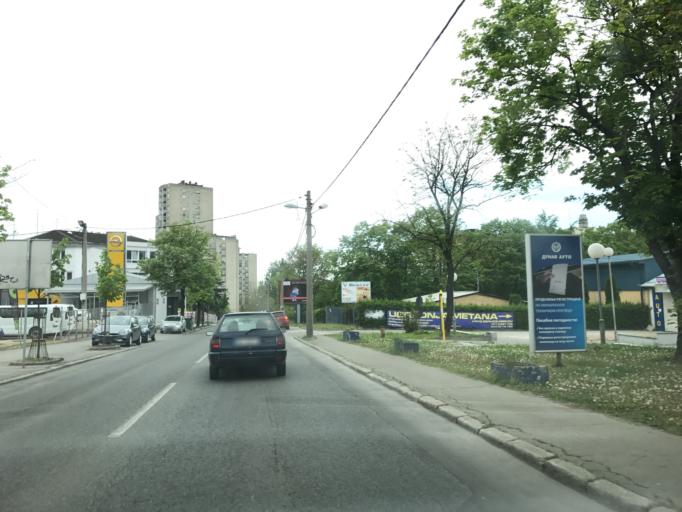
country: RS
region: Central Serbia
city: Belgrade
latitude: 44.8164
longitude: 20.4882
